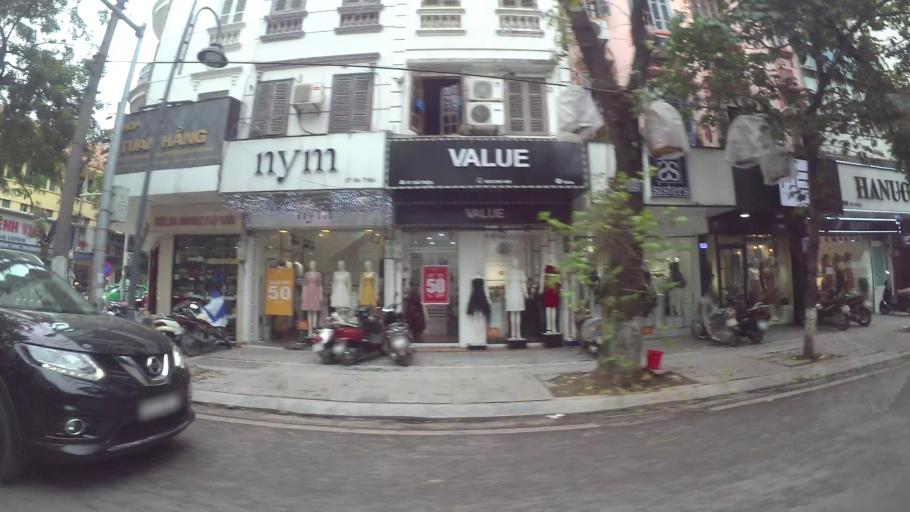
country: VN
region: Ha Noi
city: Hai BaTrung
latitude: 21.0167
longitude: 105.8491
